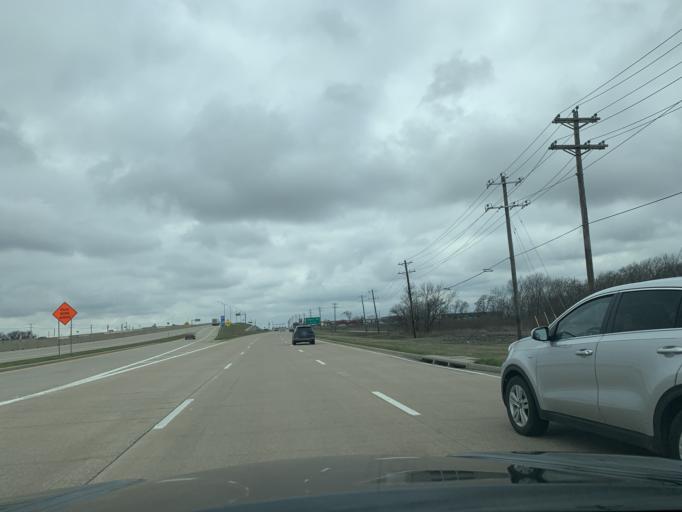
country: US
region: Texas
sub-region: Collin County
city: Allen
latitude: 33.1426
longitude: -96.6861
